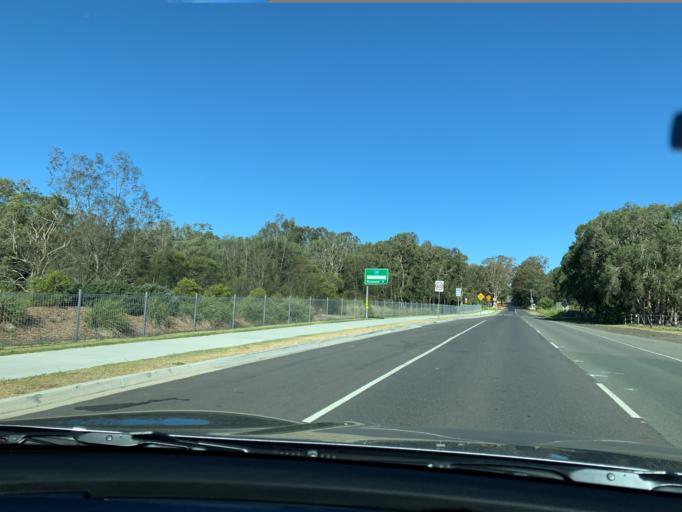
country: AU
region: Queensland
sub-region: Brisbane
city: Wynnum
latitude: -27.4258
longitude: 153.1561
